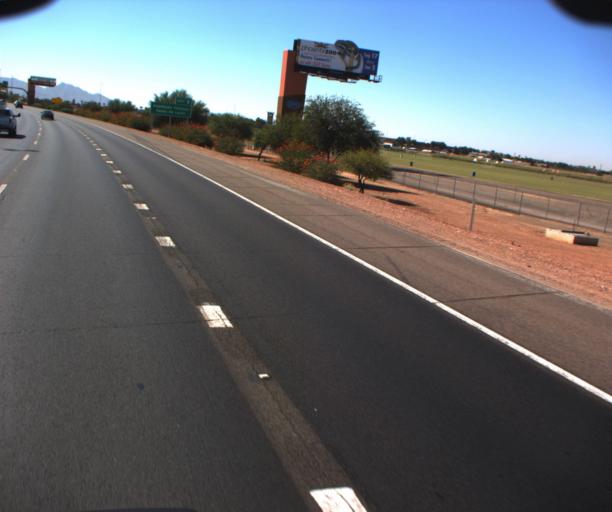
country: US
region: Arizona
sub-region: Maricopa County
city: Tolleson
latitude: 33.4722
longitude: -112.2677
